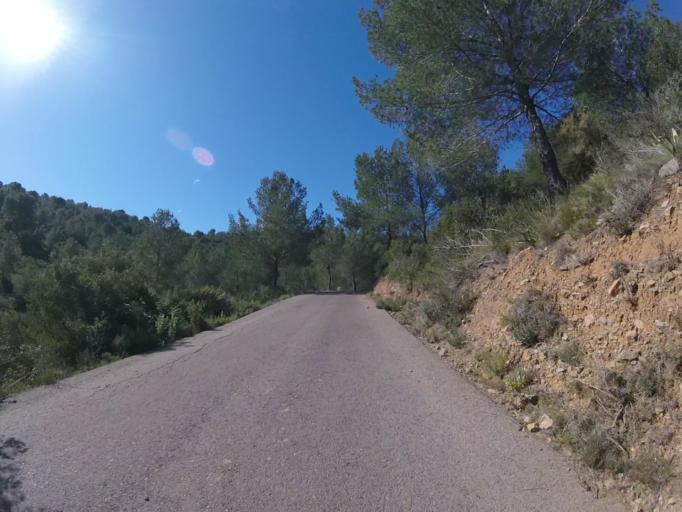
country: ES
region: Valencia
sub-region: Provincia de Castello
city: Benicassim
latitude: 40.0786
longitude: 0.0982
